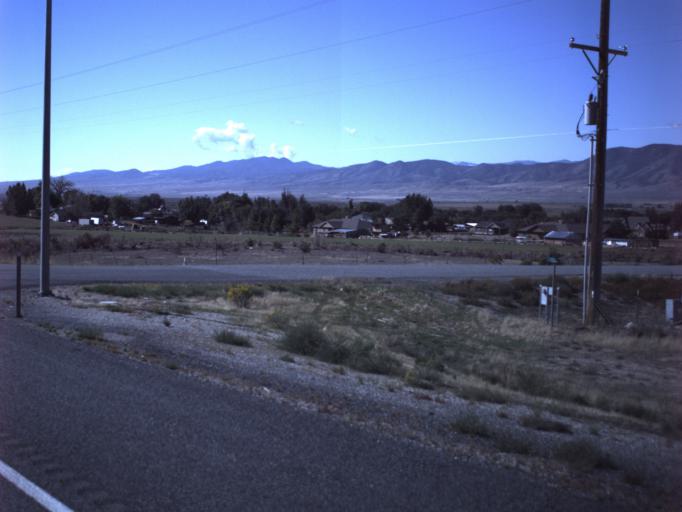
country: US
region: Utah
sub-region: Sanpete County
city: Gunnison
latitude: 39.2302
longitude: -111.8479
